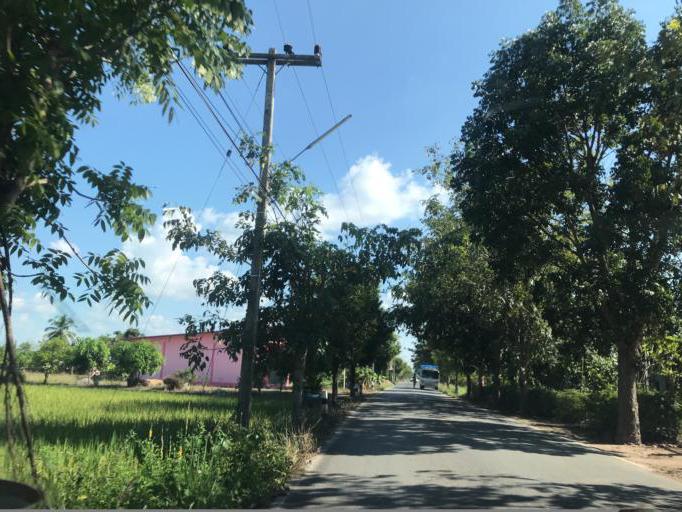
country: TH
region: Chiang Mai
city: Mae Wang
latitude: 18.5504
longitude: 98.8354
